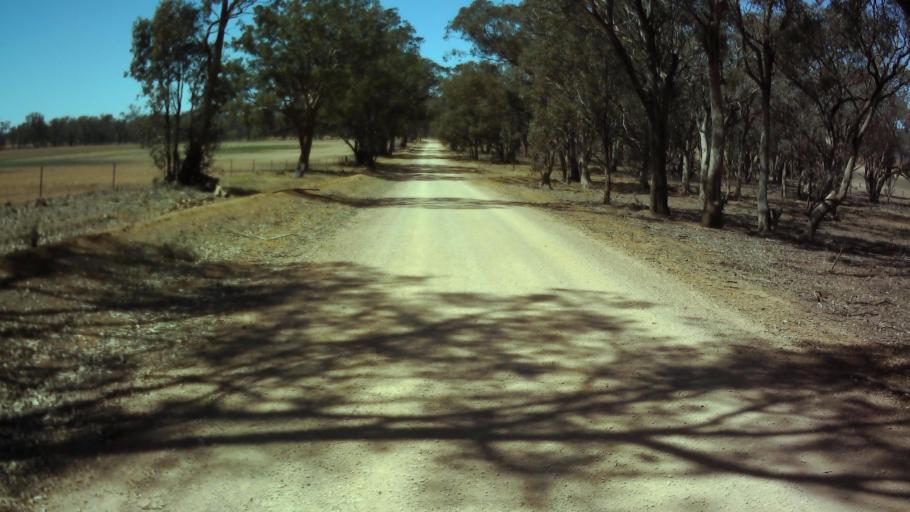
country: AU
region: New South Wales
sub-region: Weddin
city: Grenfell
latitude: -33.9334
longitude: 148.0771
